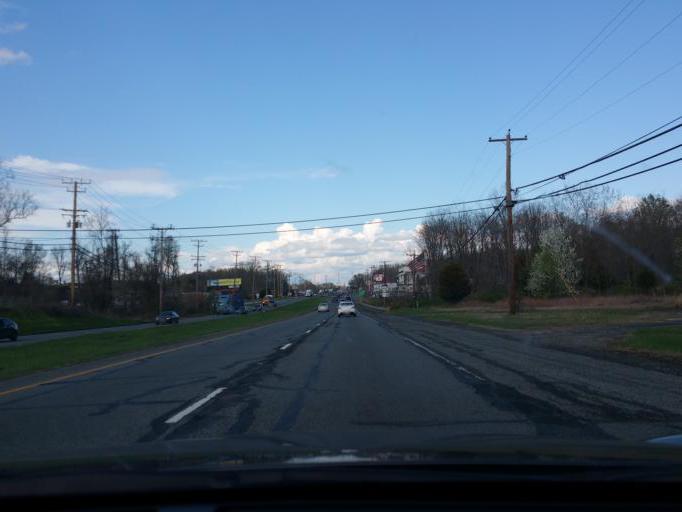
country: US
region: Maryland
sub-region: Harford County
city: Havre de Grace
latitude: 39.5311
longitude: -76.1243
